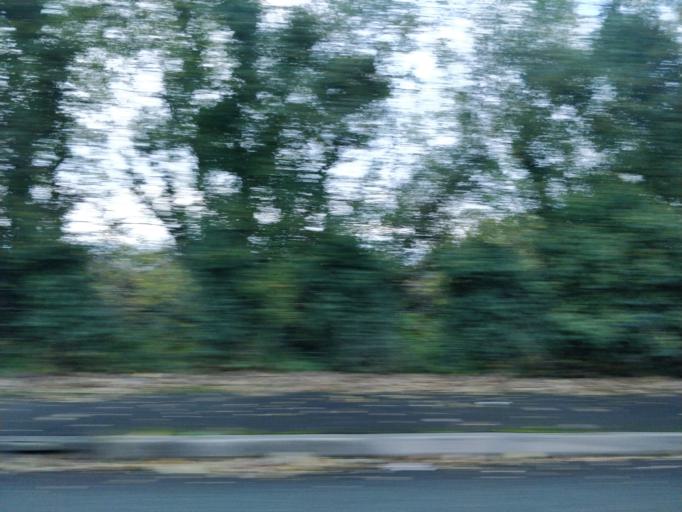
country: GB
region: England
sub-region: Sefton
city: Southport
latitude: 53.6635
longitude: -2.9833
